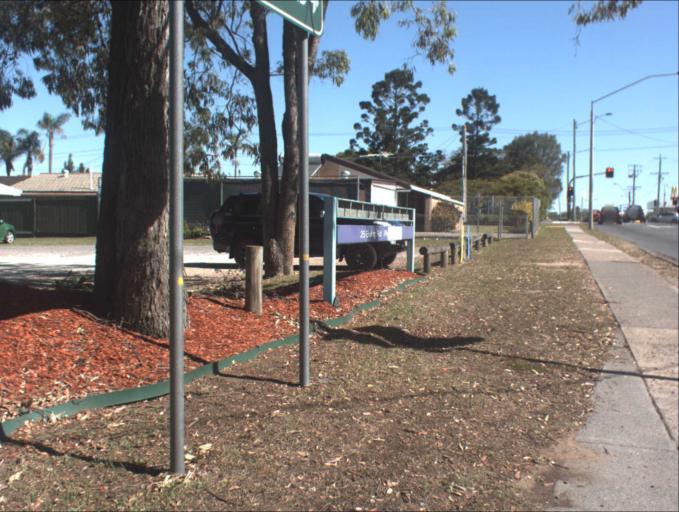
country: AU
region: Queensland
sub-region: Logan
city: Logan City
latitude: -27.6392
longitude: 153.1077
